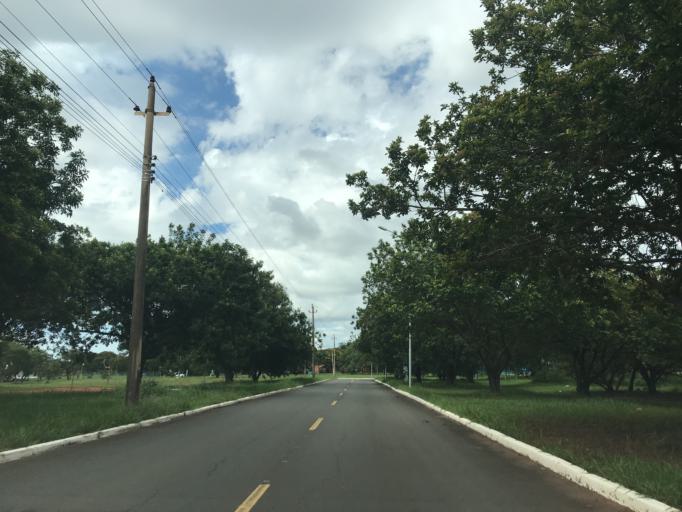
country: BR
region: Federal District
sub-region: Brasilia
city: Brasilia
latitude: -15.8073
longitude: -47.8773
